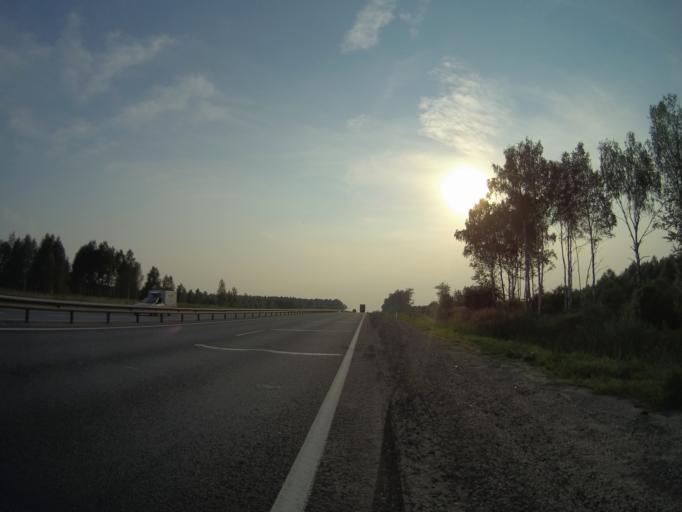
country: RU
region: Vladimir
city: Melekhovo
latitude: 56.2044
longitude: 41.1583
